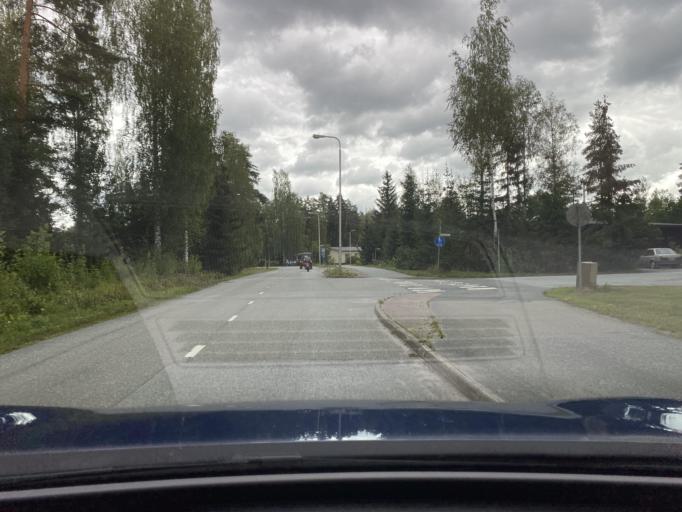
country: FI
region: Pirkanmaa
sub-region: Lounais-Pirkanmaa
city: Vammala
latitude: 61.3327
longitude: 22.9322
